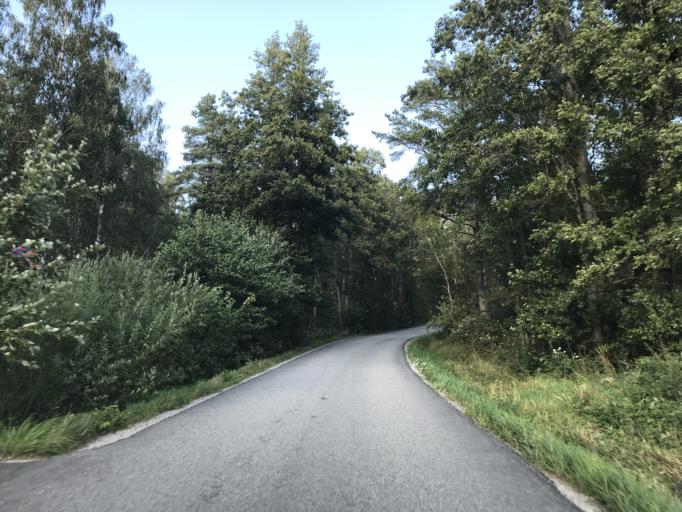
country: SE
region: Stockholm
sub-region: Norrtalje Kommun
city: Bjorko
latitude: 59.8577
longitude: 19.0240
